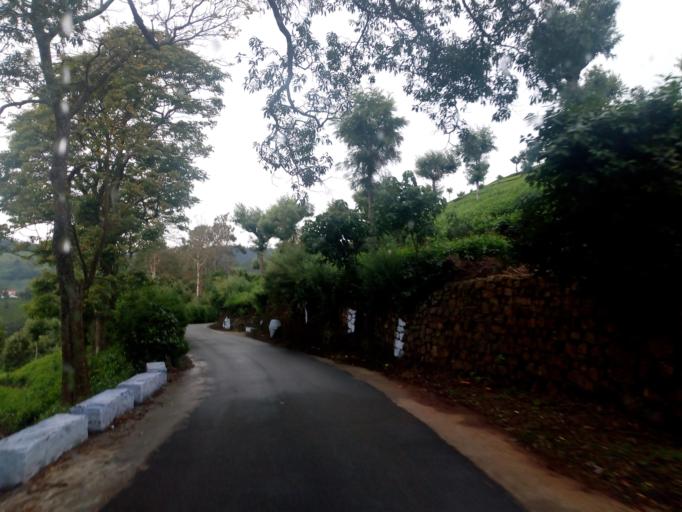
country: IN
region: Tamil Nadu
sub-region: Nilgiri
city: Wellington
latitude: 11.3610
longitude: 76.8441
